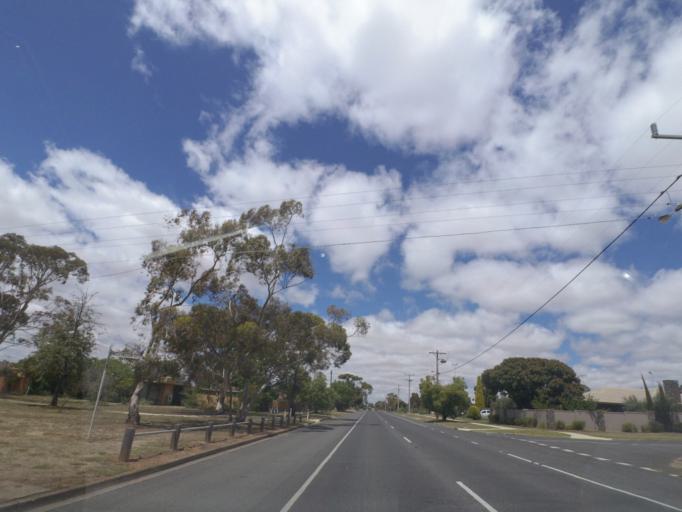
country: AU
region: Victoria
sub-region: Moorabool
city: Bacchus Marsh
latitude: -37.6554
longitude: 144.4429
